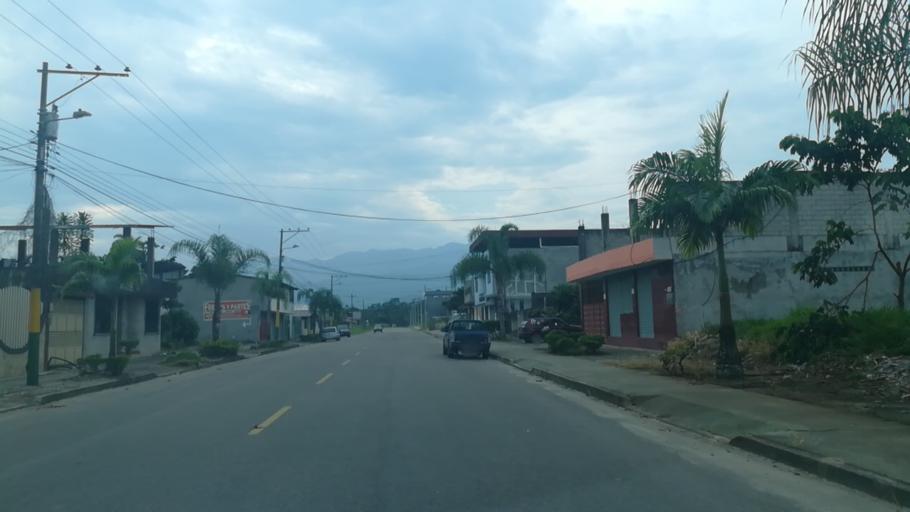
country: EC
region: Napo
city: Tena
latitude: -0.9841
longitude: -77.8228
